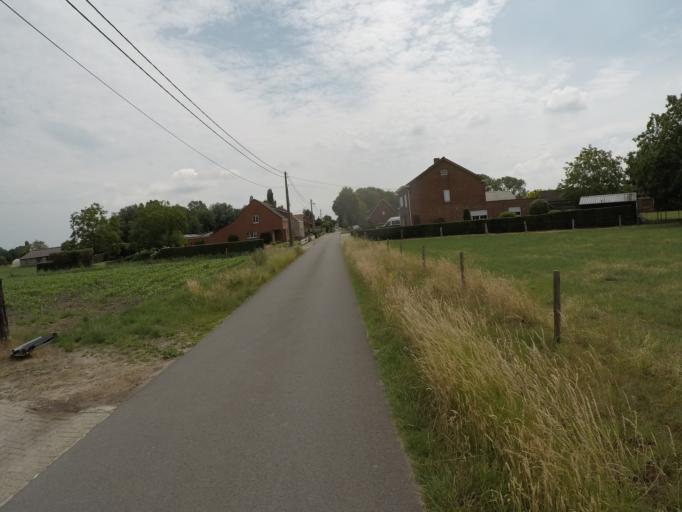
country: BE
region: Flanders
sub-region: Provincie Antwerpen
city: Essen
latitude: 51.4344
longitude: 4.5268
